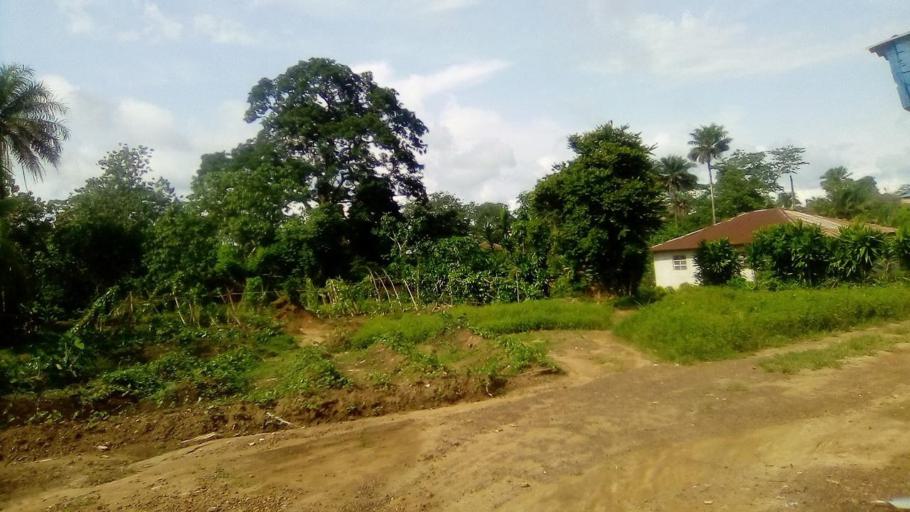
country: SL
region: Southern Province
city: Pujehun
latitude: 7.3673
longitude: -11.7267
